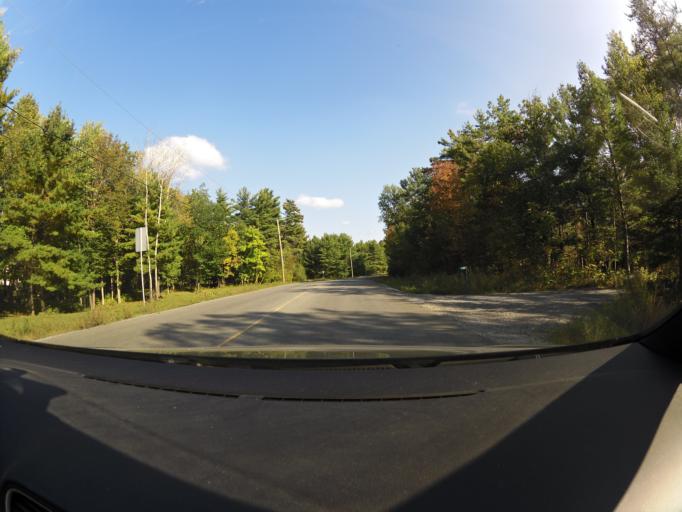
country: CA
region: Ontario
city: Arnprior
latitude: 45.4441
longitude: -76.2639
